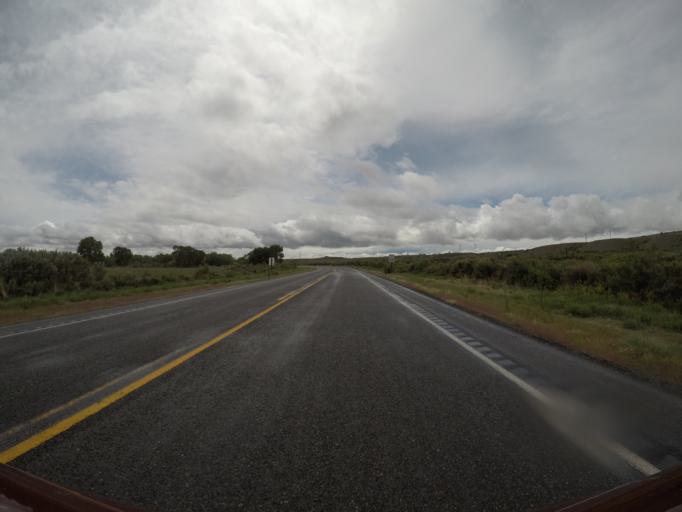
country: US
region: Wyoming
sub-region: Big Horn County
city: Lovell
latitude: 44.8661
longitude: -108.3289
